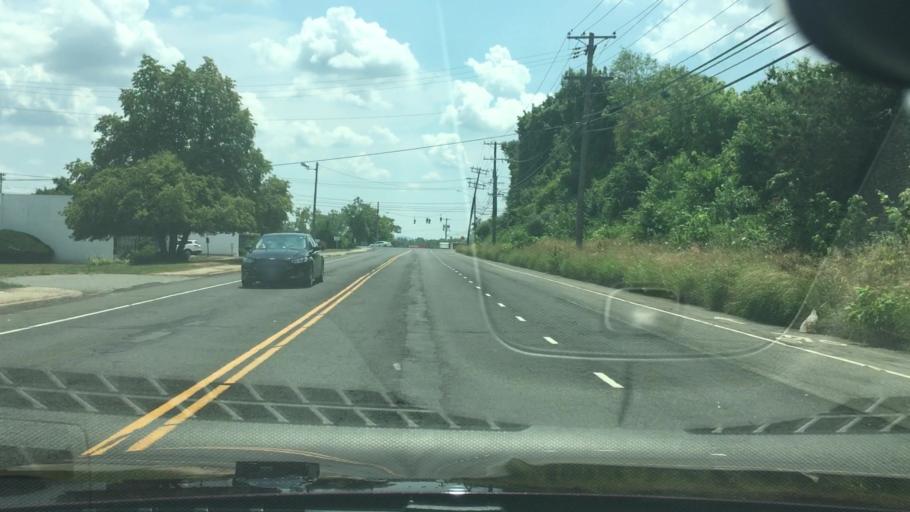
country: US
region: Connecticut
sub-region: Hartford County
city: Kensington
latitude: 41.6556
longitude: -72.7531
